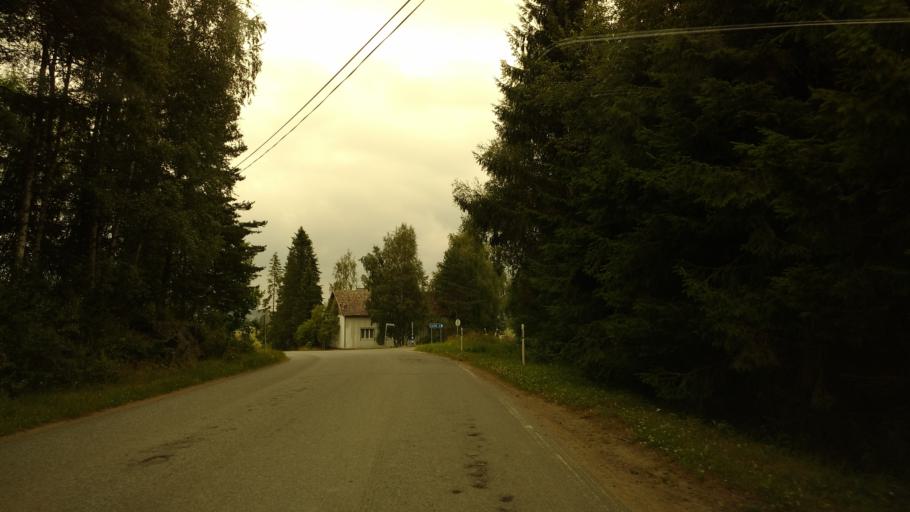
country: FI
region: Haeme
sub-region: Forssa
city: Ypaejae
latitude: 60.7801
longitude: 23.2668
